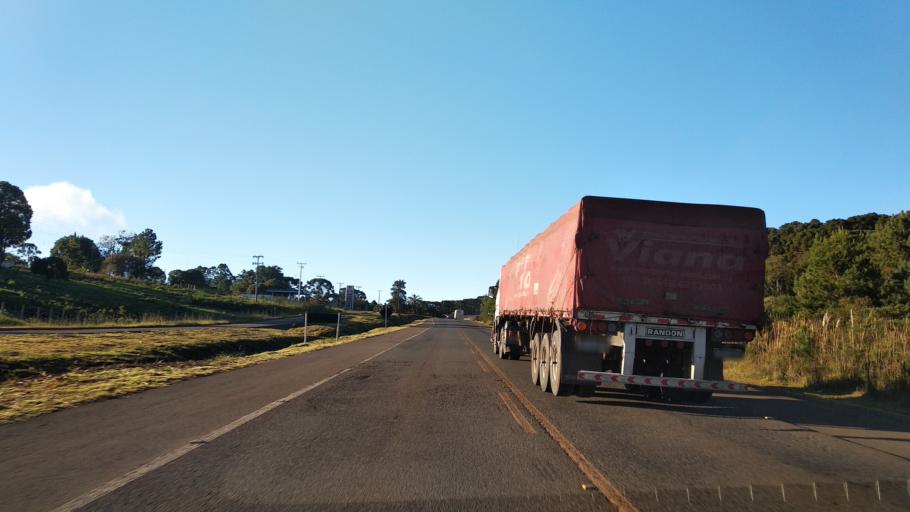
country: BR
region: Santa Catarina
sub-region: Correia Pinto
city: Correia Pinto
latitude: -27.6438
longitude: -50.5947
